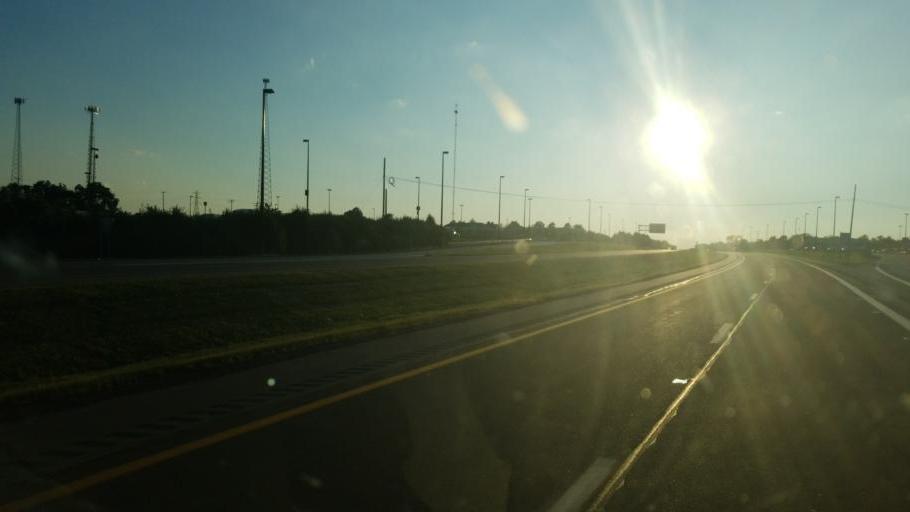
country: US
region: Ohio
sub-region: Mahoning County
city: New Middletown
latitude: 40.9390
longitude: -80.5826
